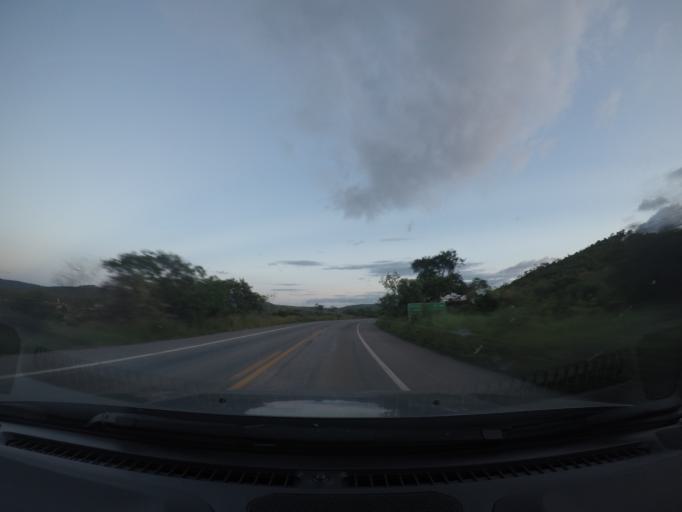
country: BR
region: Bahia
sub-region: Seabra
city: Seabra
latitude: -12.4295
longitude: -41.7591
